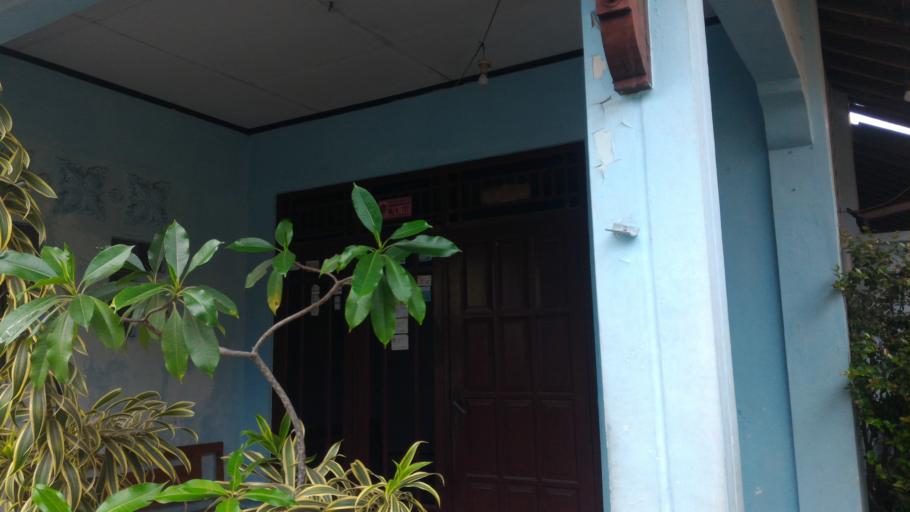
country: ID
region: Daerah Istimewa Yogyakarta
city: Kasihan
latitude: -7.8189
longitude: 110.3582
